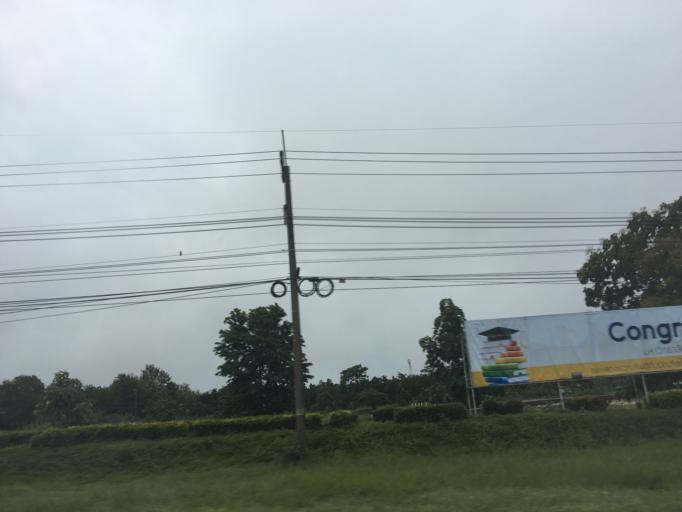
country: TH
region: Kanchanaburi
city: Sai Yok
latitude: 14.1306
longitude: 99.1625
